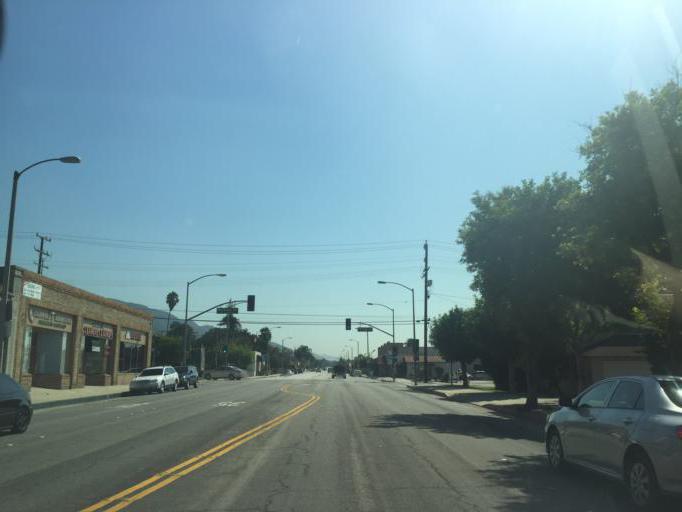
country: US
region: California
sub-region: Los Angeles County
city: Monrovia
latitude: 34.1512
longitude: -118.0105
